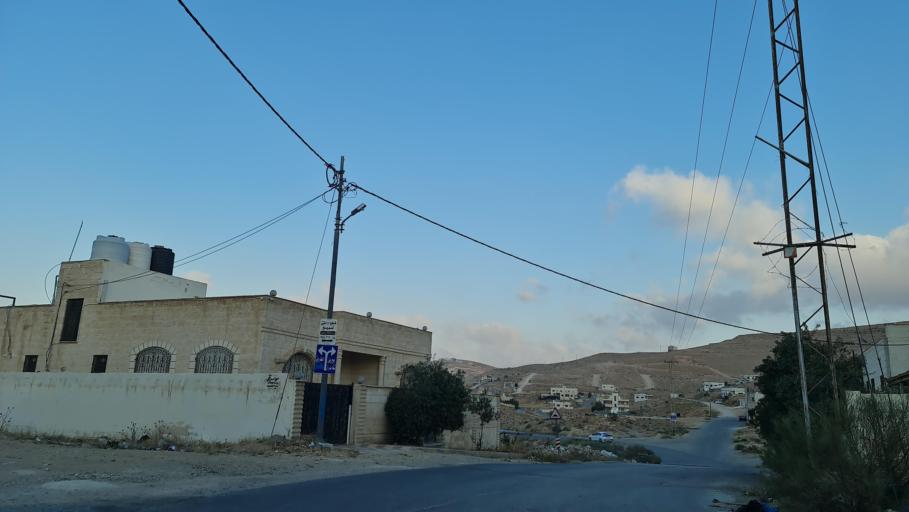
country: JO
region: Zarqa
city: Zarqa
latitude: 32.0829
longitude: 36.0528
